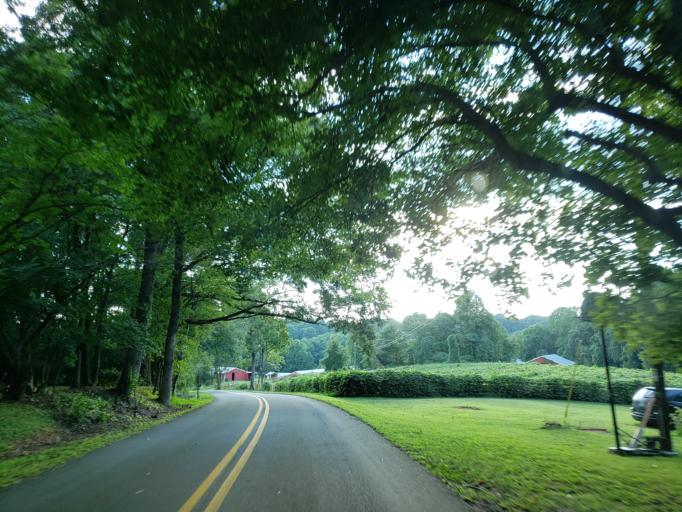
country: US
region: Georgia
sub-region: Cherokee County
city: Ball Ground
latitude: 34.3610
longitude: -84.4686
